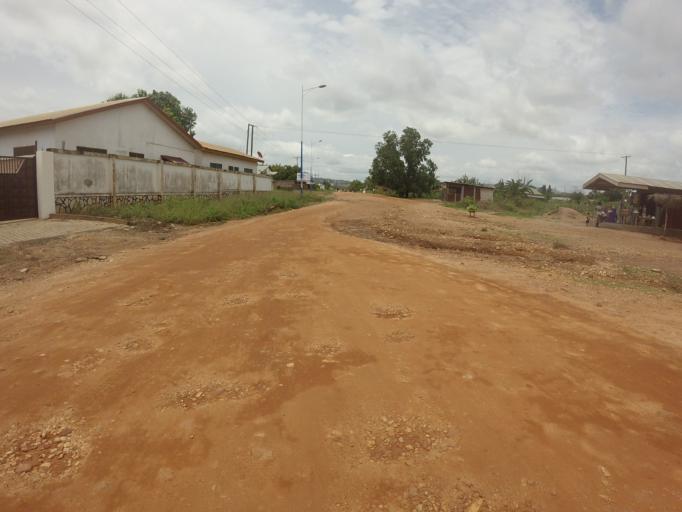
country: GH
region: Volta
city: Ho
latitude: 6.5798
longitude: 0.4634
